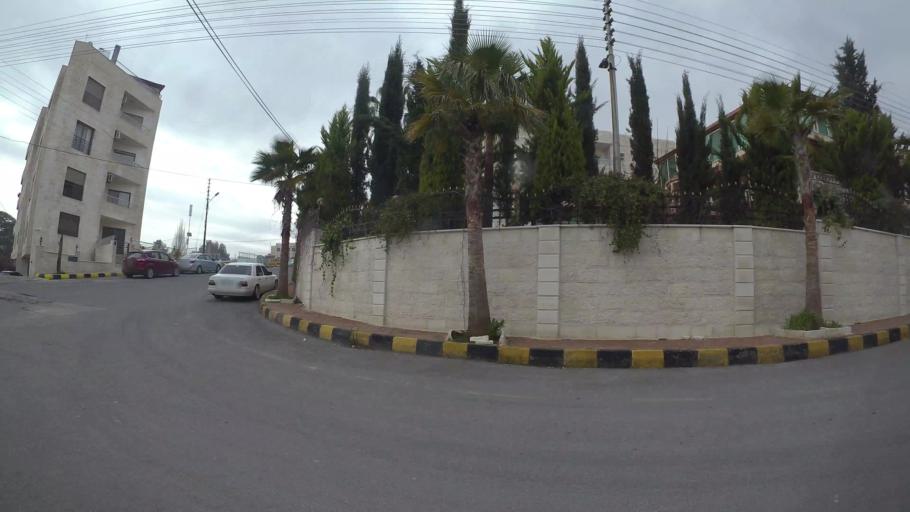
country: JO
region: Amman
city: Umm as Summaq
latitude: 31.9050
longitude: 35.8520
